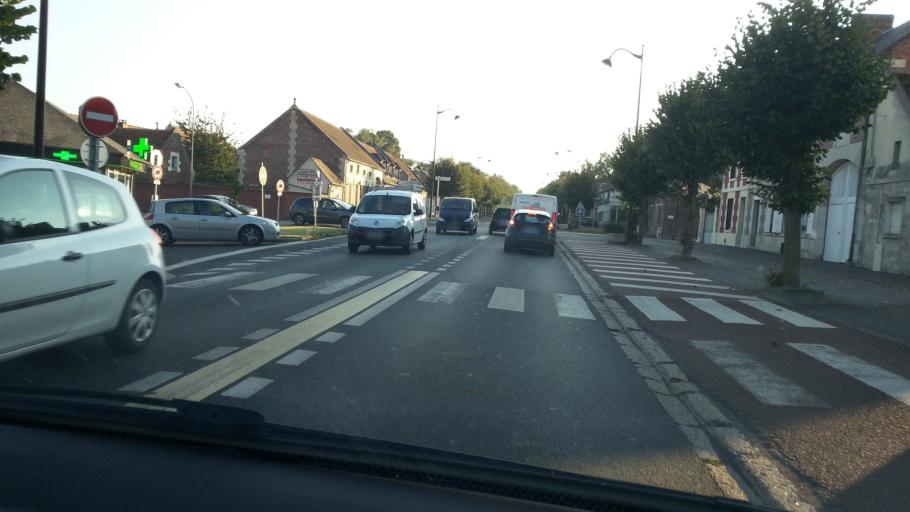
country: FR
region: Picardie
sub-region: Departement de l'Oise
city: Estrees-Saint-Denis
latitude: 49.4236
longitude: 2.6363
